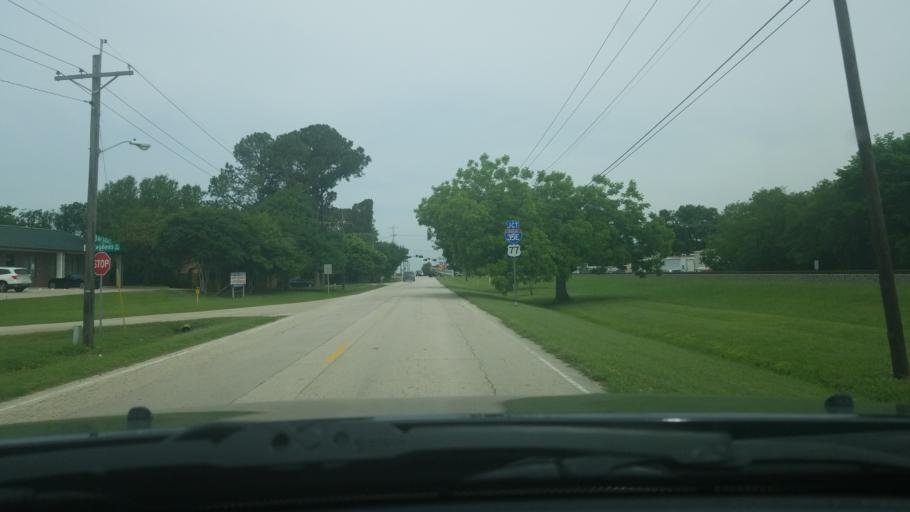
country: US
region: Texas
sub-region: Denton County
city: Lake Dallas
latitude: 33.1209
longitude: -97.0313
